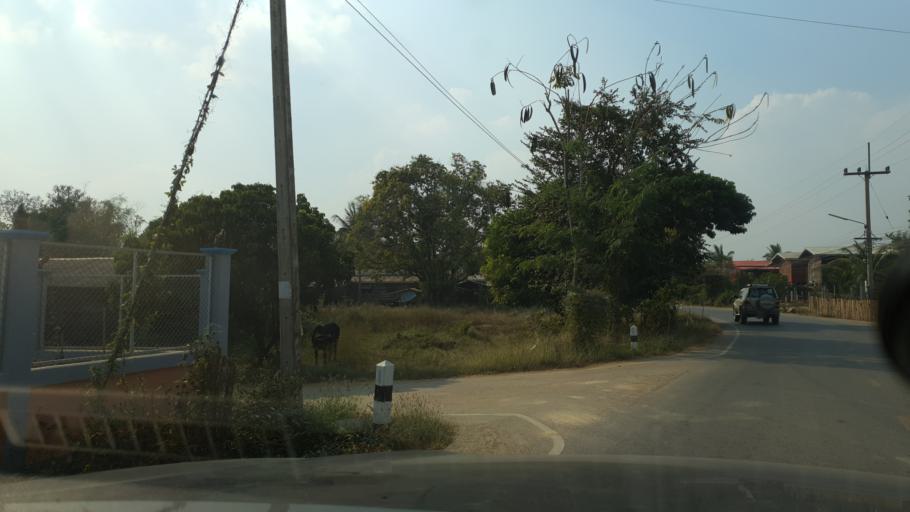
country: TH
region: Sukhothai
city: Ban Dan Lan Hoi
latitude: 17.1132
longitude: 99.5424
